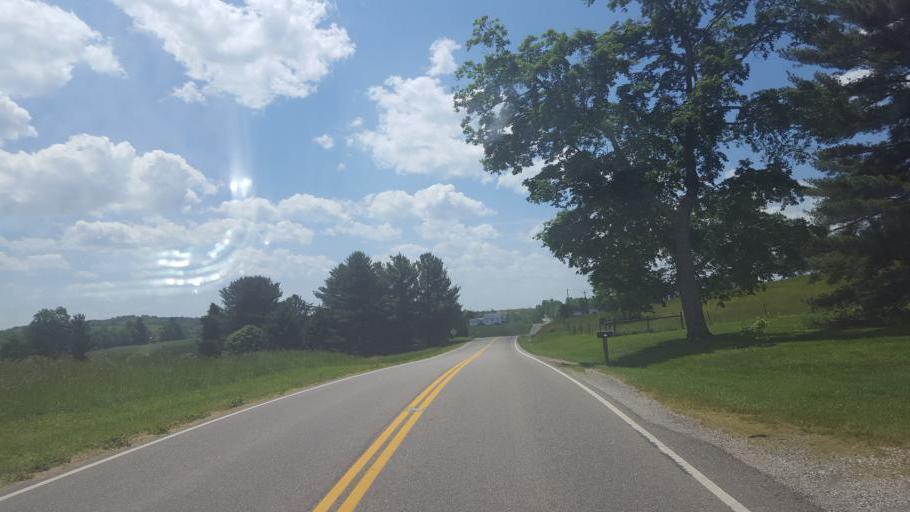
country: US
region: Ohio
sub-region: Jackson County
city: Oak Hill
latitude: 38.8384
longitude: -82.3925
